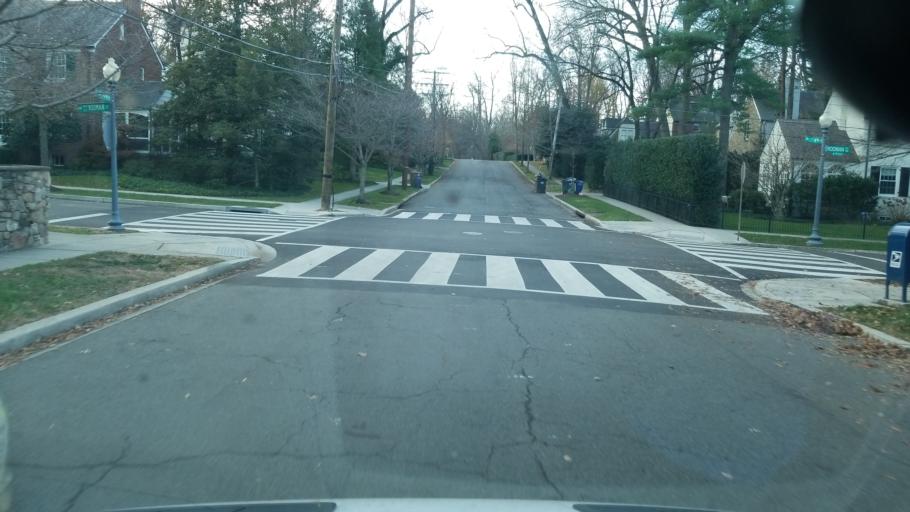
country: US
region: Maryland
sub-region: Montgomery County
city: Brookmont
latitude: 38.9396
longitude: -77.0968
